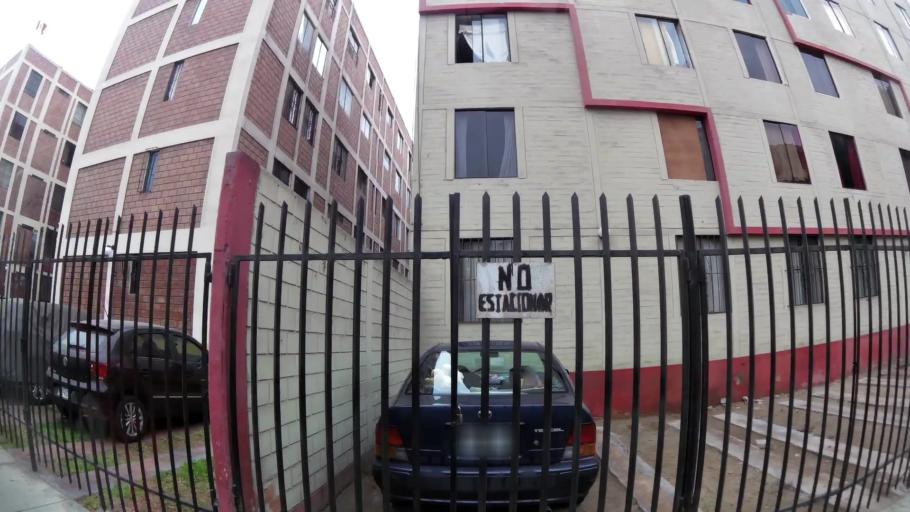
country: PE
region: Lima
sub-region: Lima
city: Surco
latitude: -12.1443
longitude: -77.0013
